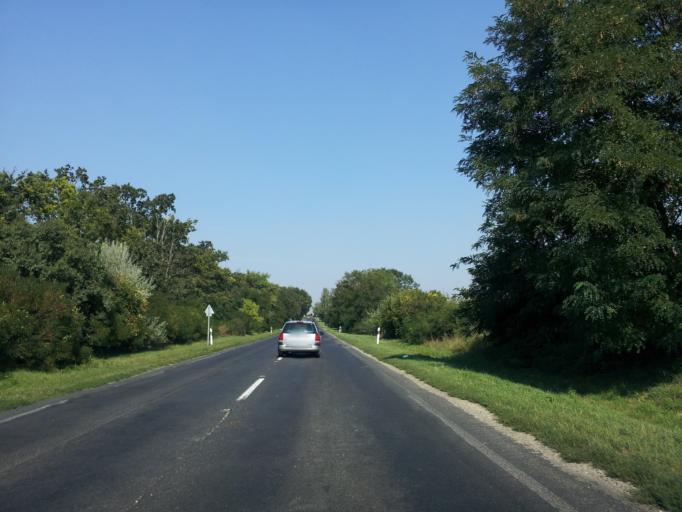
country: HU
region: Somogy
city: Balatonszabadi
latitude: 46.9437
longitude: 18.1677
